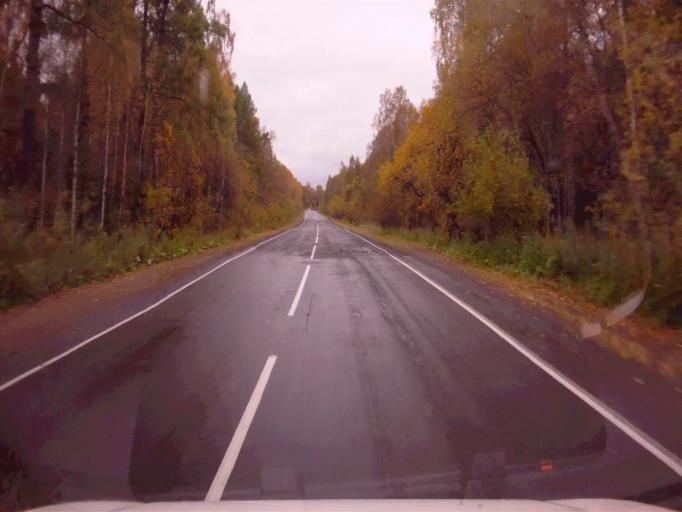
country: RU
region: Chelyabinsk
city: Nizhniy Ufaley
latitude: 56.0647
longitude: 60.0008
